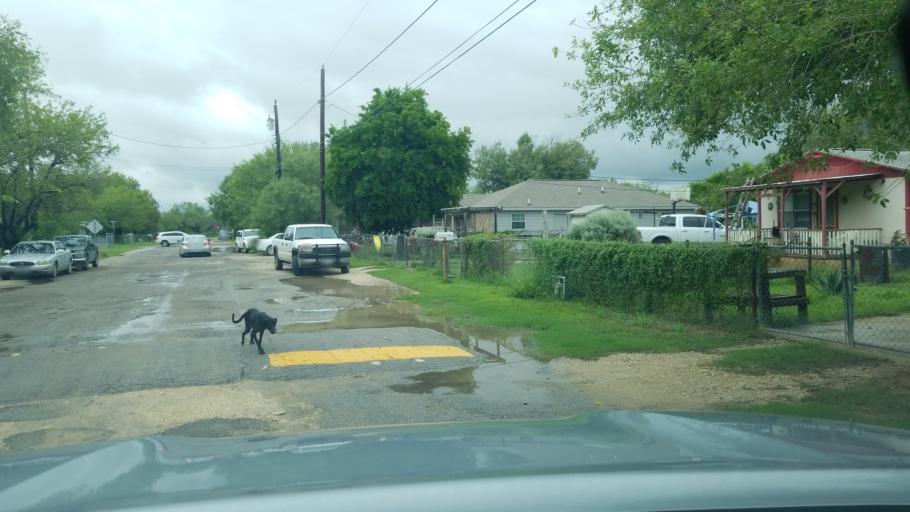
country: US
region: Texas
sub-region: Dimmit County
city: Carrizo Springs
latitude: 28.5310
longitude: -99.8478
